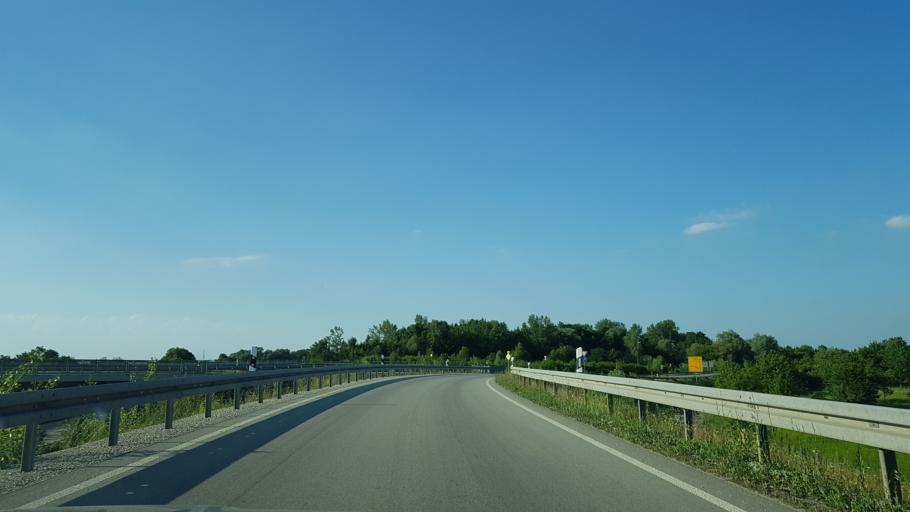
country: DE
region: Bavaria
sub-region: Upper Bavaria
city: Ismaning
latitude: 48.2553
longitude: 11.7069
